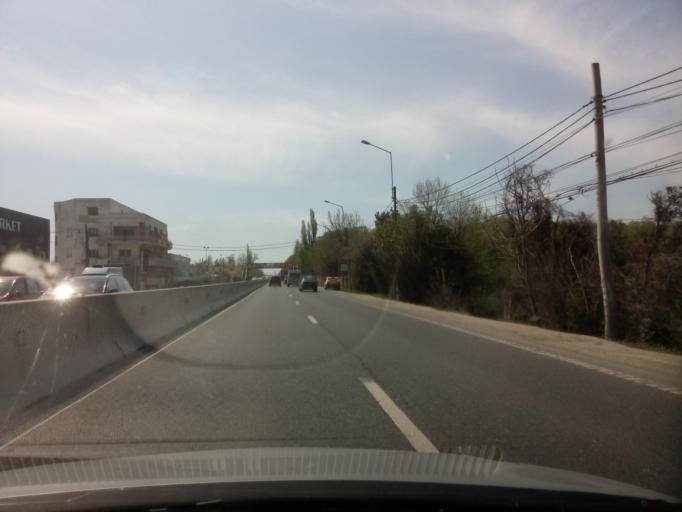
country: RO
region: Ilfov
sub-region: Comuna Corbeanca
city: Corbeanca
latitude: 44.5816
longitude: 26.0703
